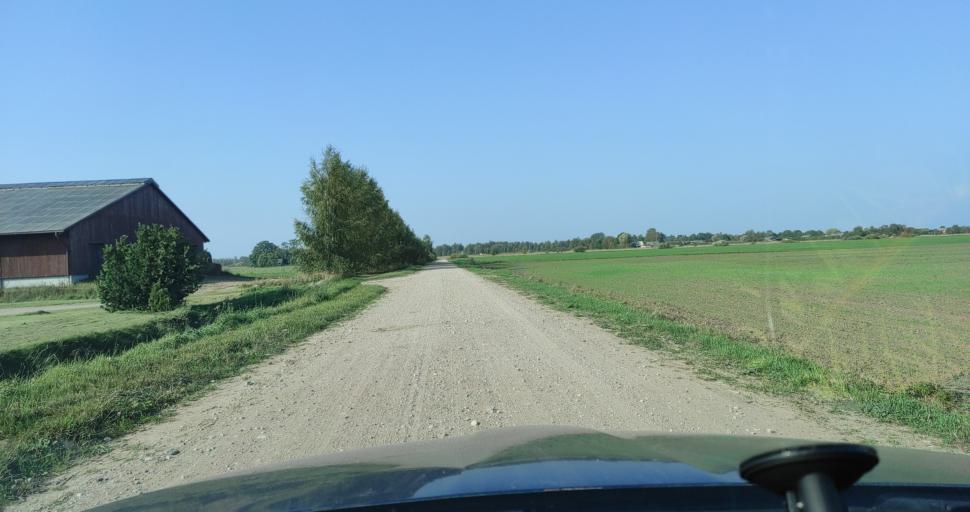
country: LV
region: Ventspils Rajons
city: Piltene
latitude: 57.2238
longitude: 21.6295
